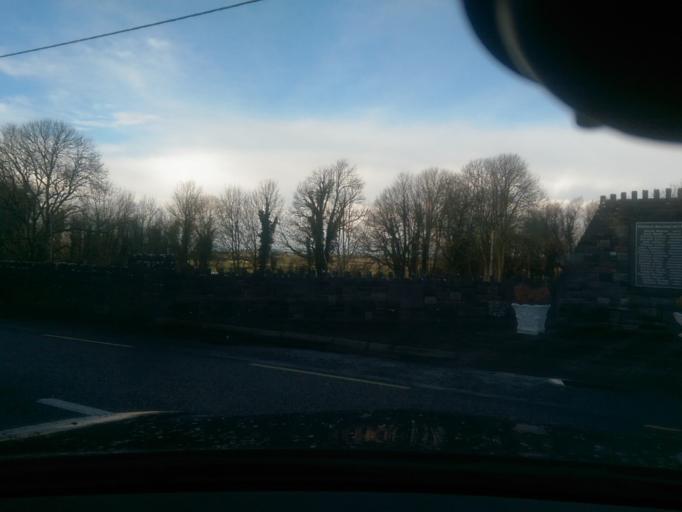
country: IE
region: Connaught
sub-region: County Galway
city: Athenry
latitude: 53.4212
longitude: -8.5721
